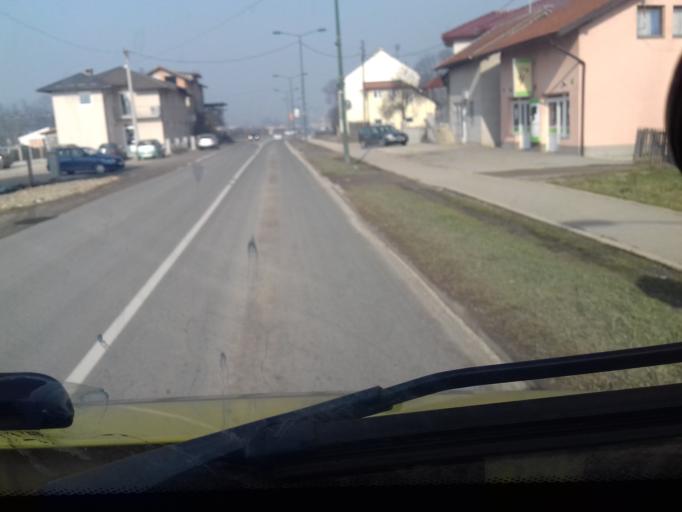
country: BA
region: Federation of Bosnia and Herzegovina
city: Ilijas
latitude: 43.9549
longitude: 18.2645
